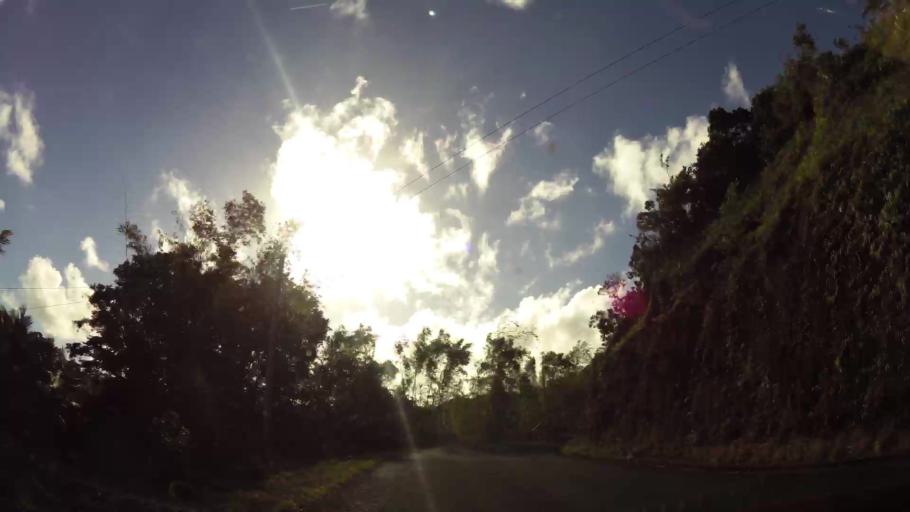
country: DM
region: Saint John
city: Portsmouth
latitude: 15.5797
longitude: -61.4176
